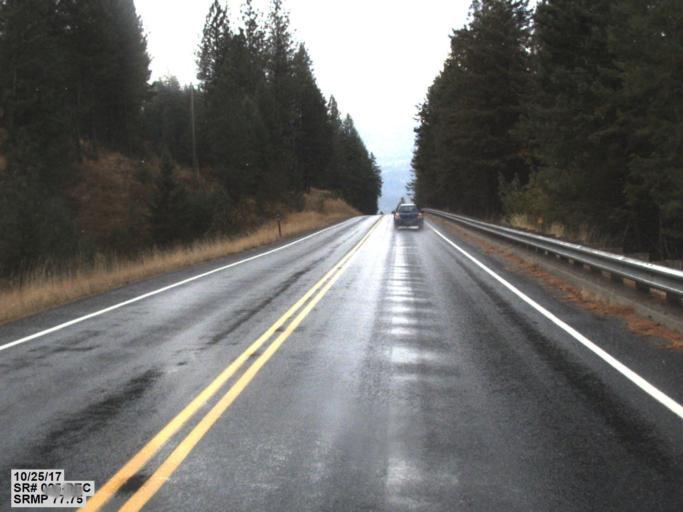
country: US
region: Washington
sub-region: Stevens County
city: Kettle Falls
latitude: 48.5706
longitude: -118.0996
